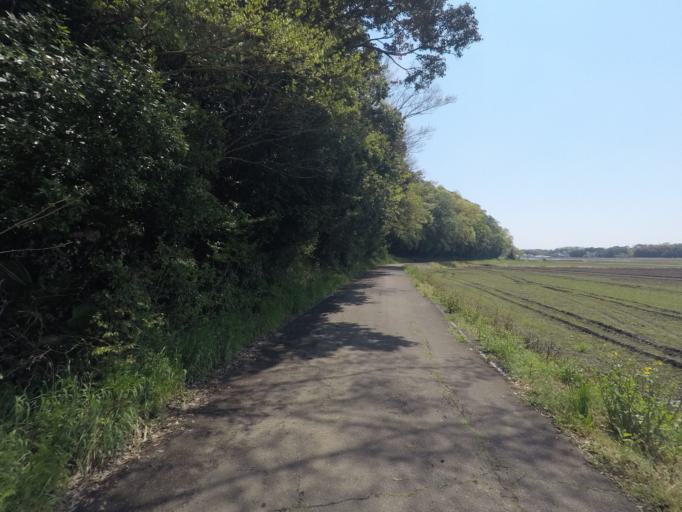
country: JP
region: Ibaraki
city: Ushiku
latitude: 35.9997
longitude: 140.1016
